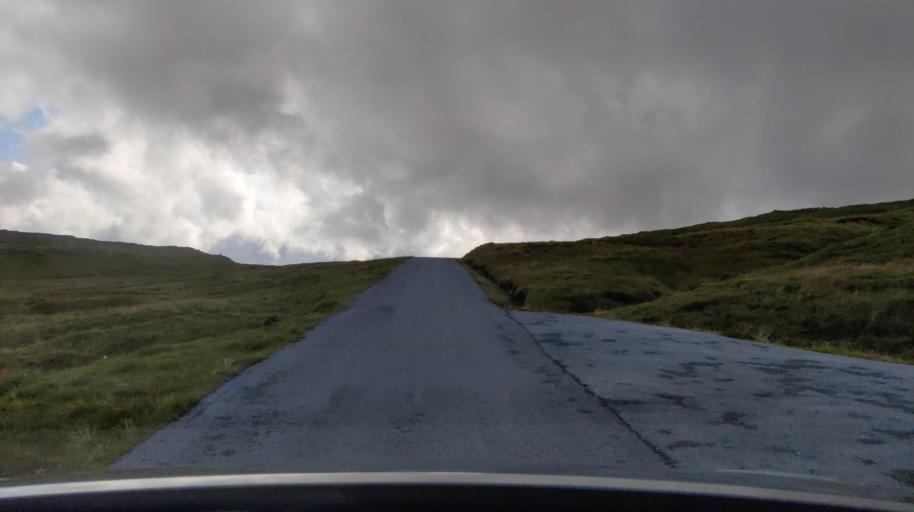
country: FO
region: Streymoy
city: Vestmanna
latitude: 62.1726
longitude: -7.1573
